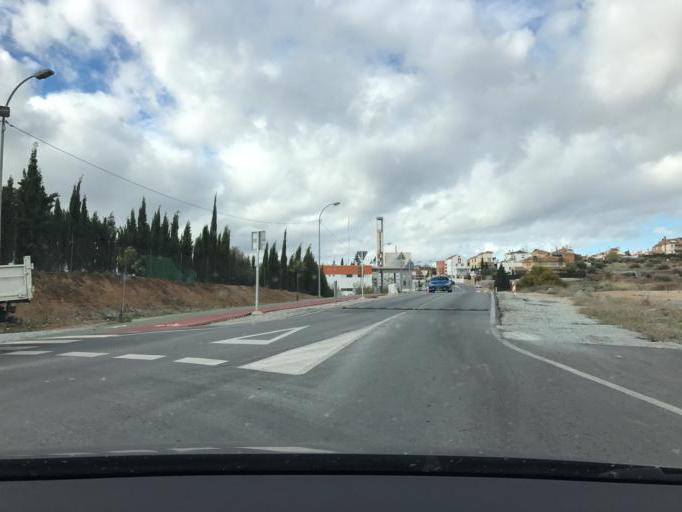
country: ES
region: Andalusia
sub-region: Provincia de Granada
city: Peligros
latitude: 37.2384
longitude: -3.6370
